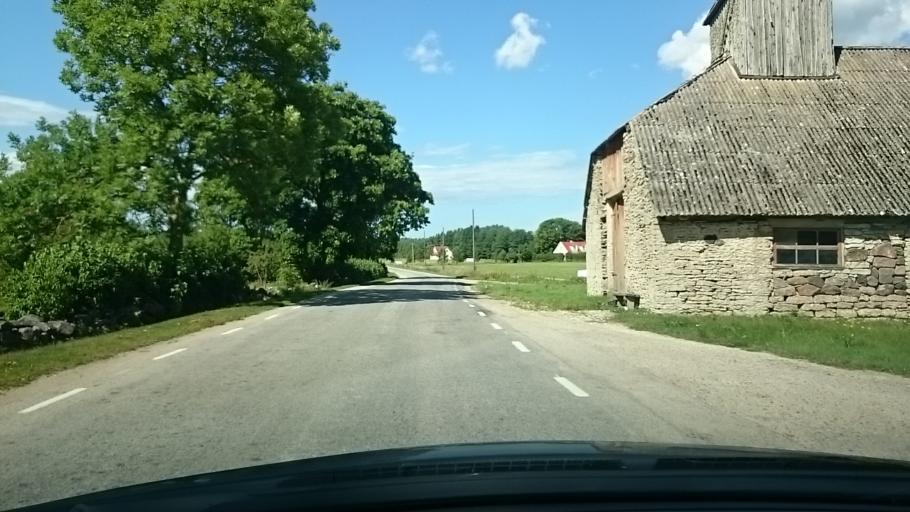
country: EE
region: Laeaene
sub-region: Haapsalu linn
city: Haapsalu
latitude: 59.0387
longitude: 23.5096
